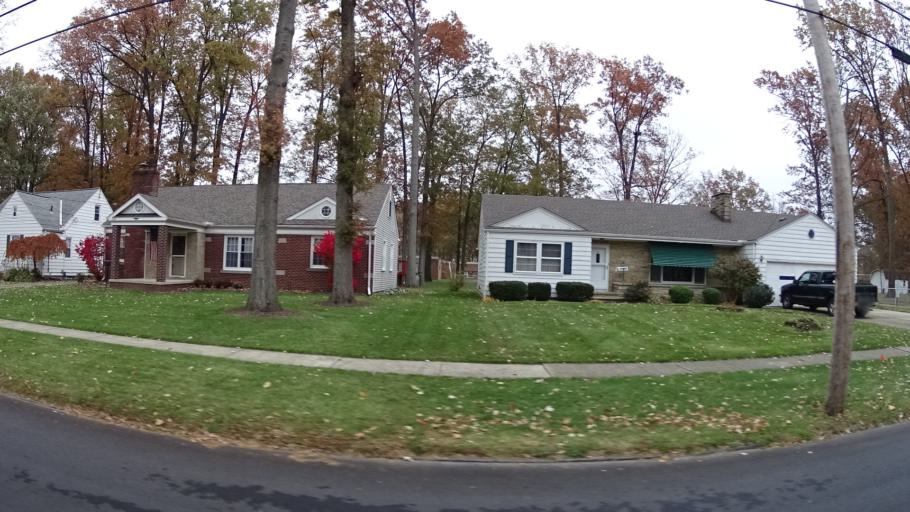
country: US
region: Ohio
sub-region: Lorain County
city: Elyria
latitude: 41.3635
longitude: -82.0918
